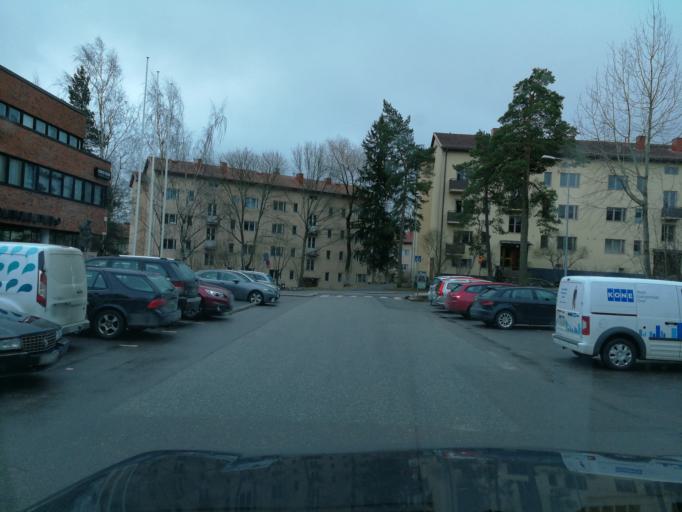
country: FI
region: Uusimaa
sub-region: Helsinki
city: Helsinki
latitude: 60.2150
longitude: 24.9561
